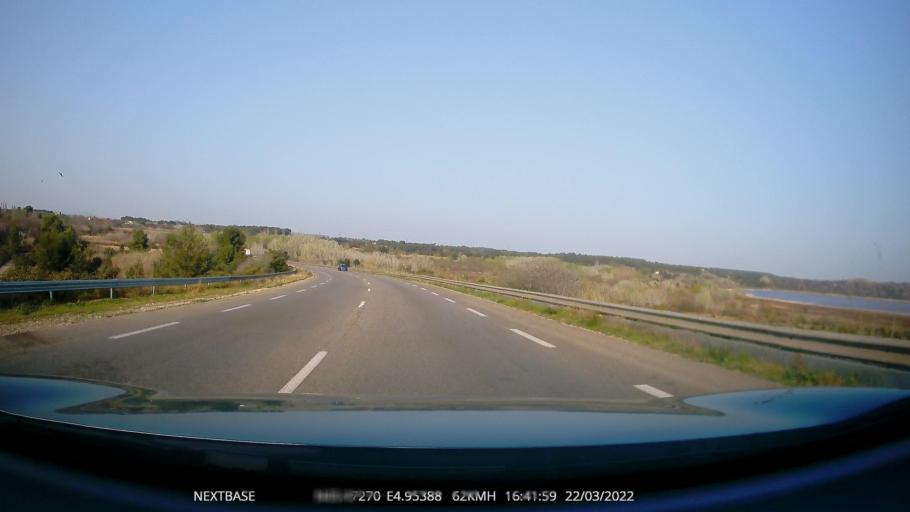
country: FR
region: Provence-Alpes-Cote d'Azur
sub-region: Departement des Bouches-du-Rhone
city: Fos-sur-Mer
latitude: 43.4726
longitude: 4.9539
